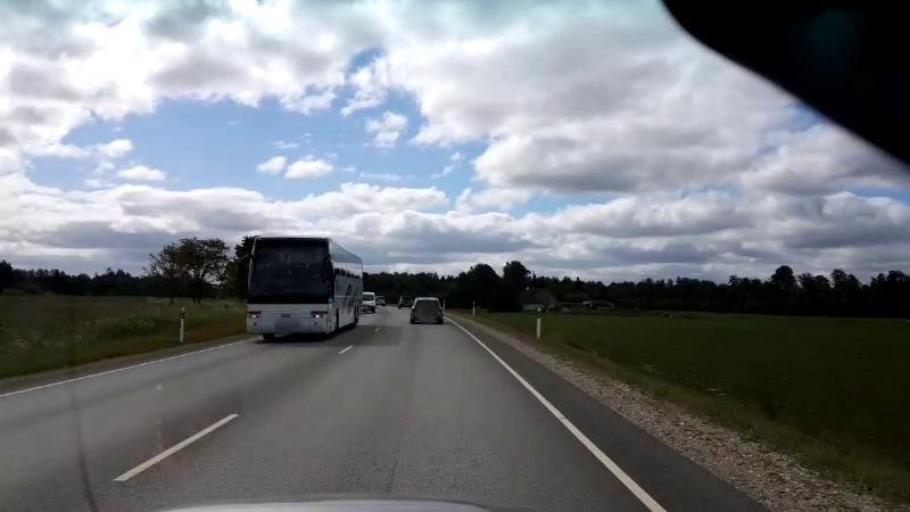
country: EE
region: Paernumaa
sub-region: Halinga vald
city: Parnu-Jaagupi
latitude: 58.5632
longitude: 24.5173
